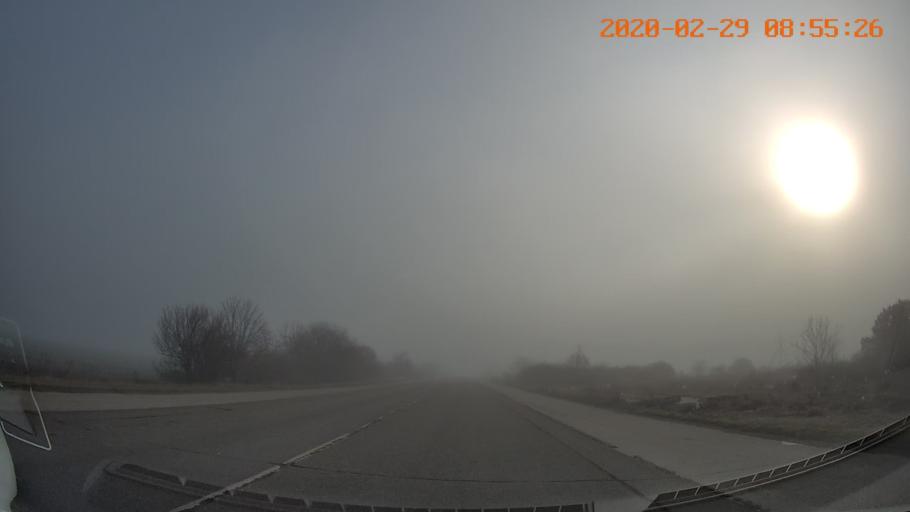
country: MD
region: Telenesti
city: Tiraspolul Nou
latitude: 46.9284
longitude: 29.5921
